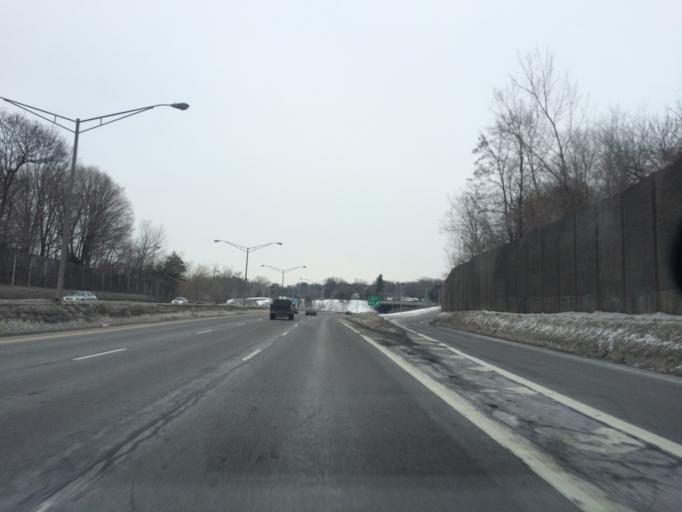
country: US
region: New York
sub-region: Monroe County
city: Brighton
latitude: 43.1317
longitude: -77.5276
